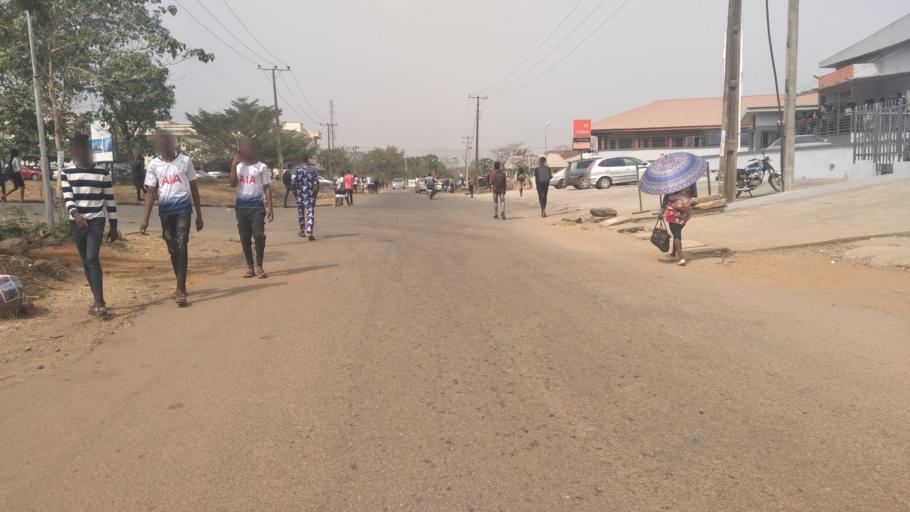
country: NG
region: Ondo
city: Ilare
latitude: 7.3009
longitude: 5.1395
